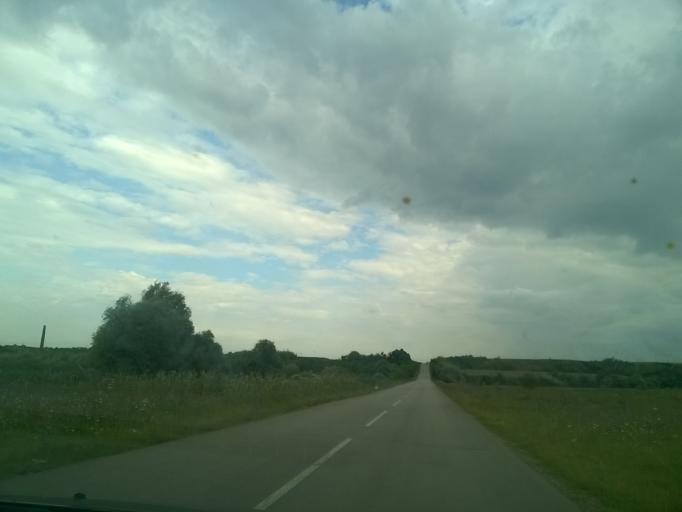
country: RS
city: Tomasevac
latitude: 45.2860
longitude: 20.6328
